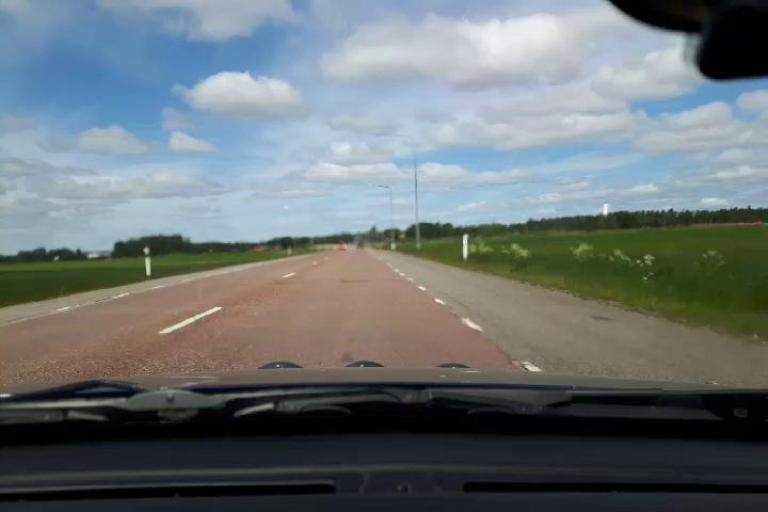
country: SE
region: Uppsala
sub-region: Osthammars Kommun
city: Bjorklinge
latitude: 60.0155
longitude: 17.5578
